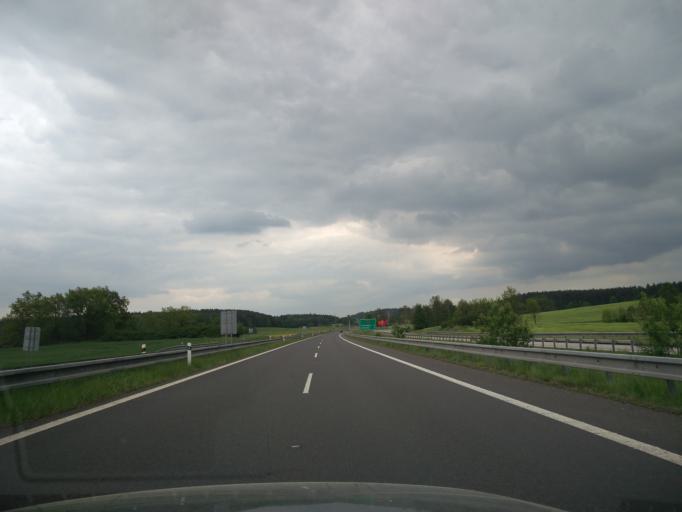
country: CZ
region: Jihocesky
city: Mirotice
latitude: 49.4106
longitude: 14.0388
